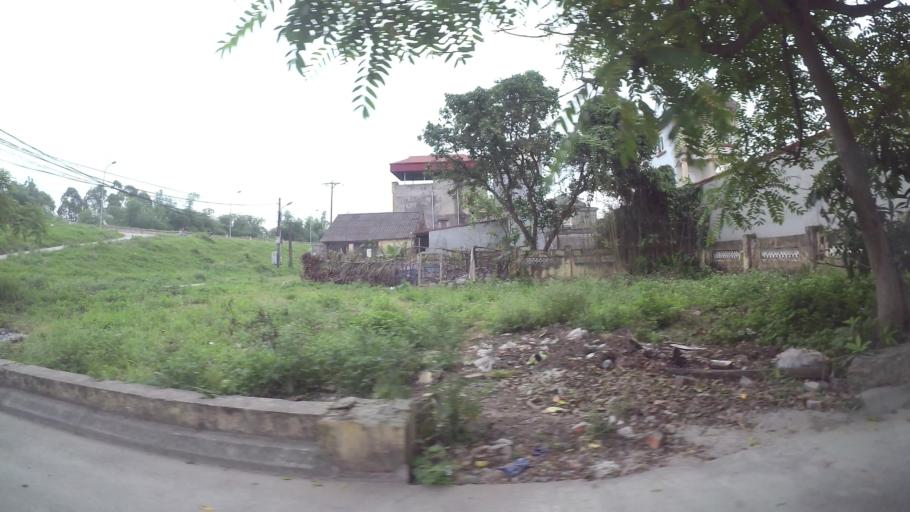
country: VN
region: Ha Noi
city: Trau Quy
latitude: 21.0447
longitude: 105.9297
